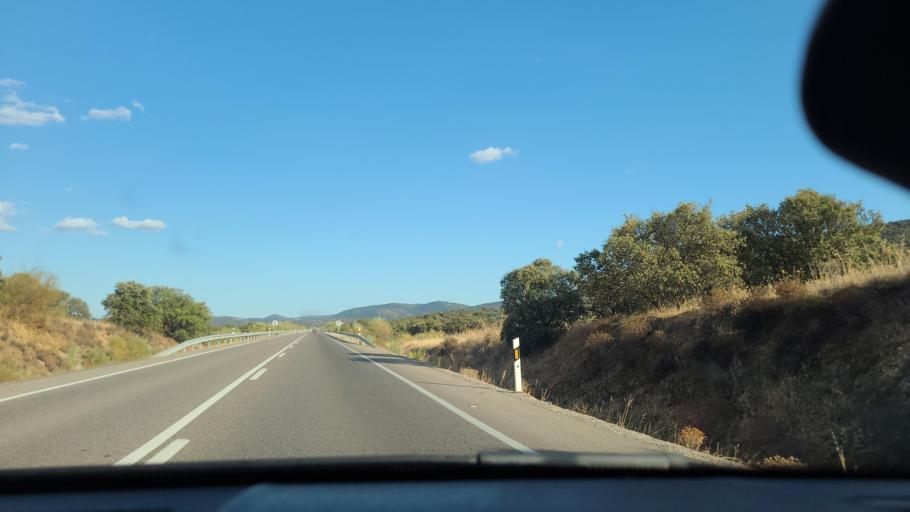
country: ES
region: Andalusia
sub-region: Province of Cordoba
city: Belmez
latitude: 38.2255
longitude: -5.1600
